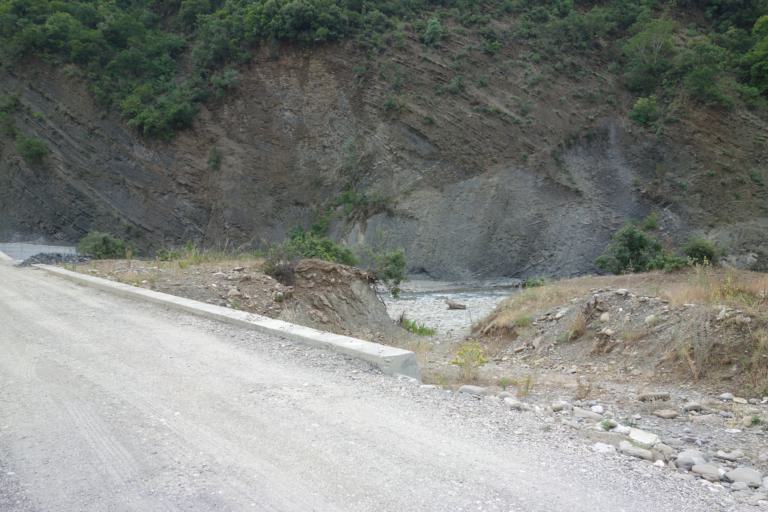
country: AL
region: Gjirokaster
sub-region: Rrethi i Permetit
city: Petran
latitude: 40.2408
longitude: 20.4305
